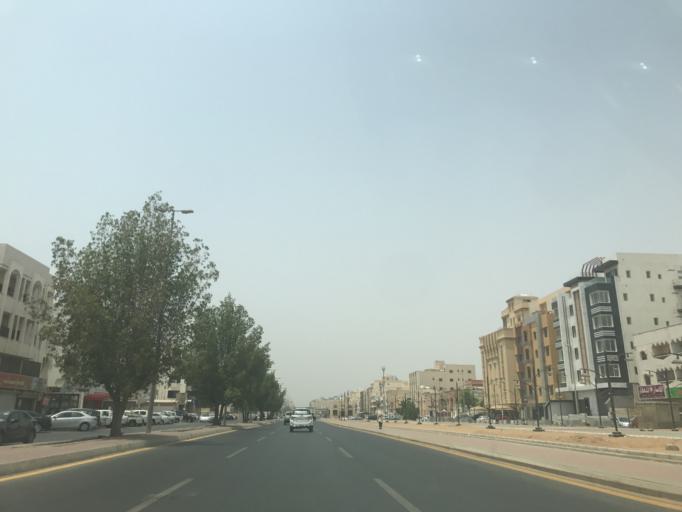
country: SA
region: Makkah
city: Jeddah
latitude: 21.5849
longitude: 39.1487
